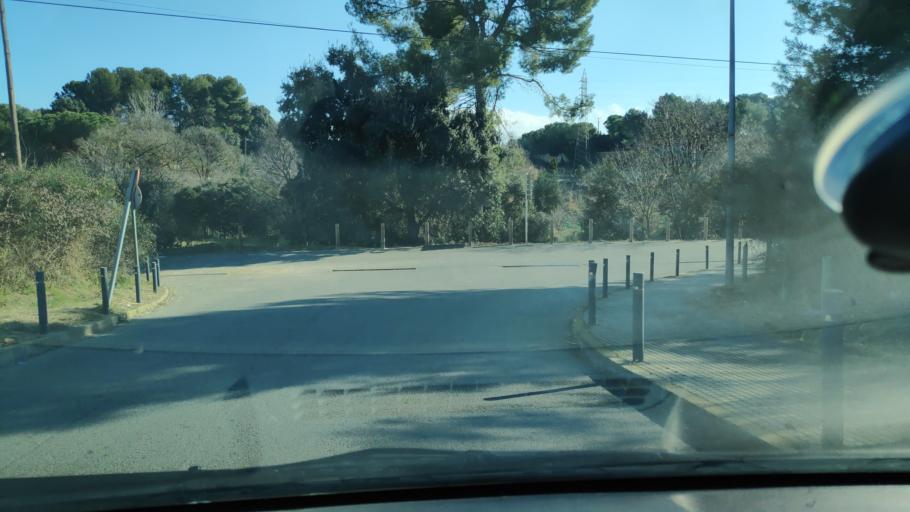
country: ES
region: Catalonia
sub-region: Provincia de Barcelona
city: Sant Quirze del Valles
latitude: 41.5571
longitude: 2.0555
